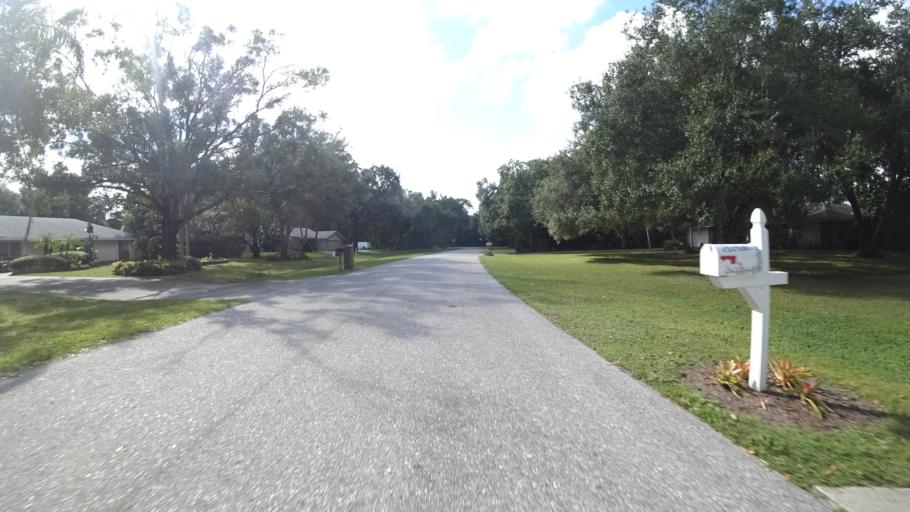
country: US
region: Florida
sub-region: Sarasota County
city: North Sarasota
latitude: 27.4078
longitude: -82.5041
